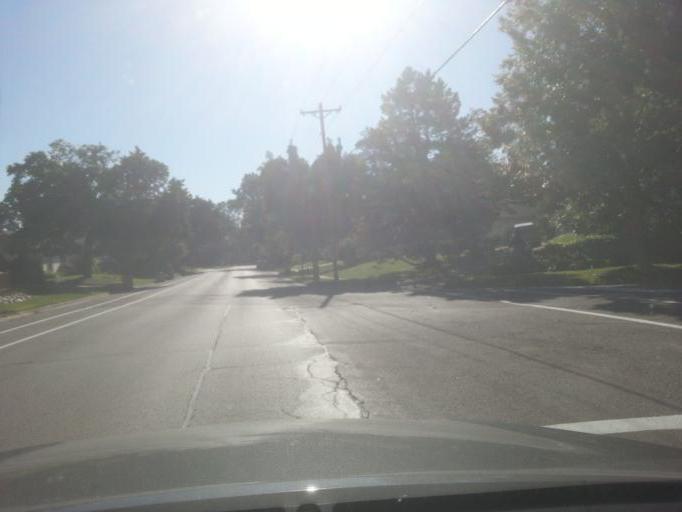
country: US
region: Wisconsin
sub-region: Dane County
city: Shorewood Hills
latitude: 43.0514
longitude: -89.4395
